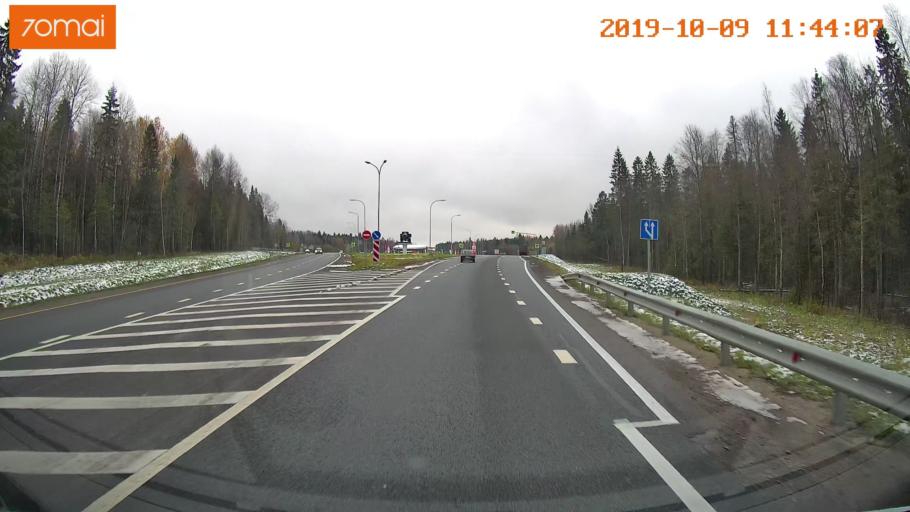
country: RU
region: Vologda
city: Gryazovets
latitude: 58.8876
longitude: 40.1897
